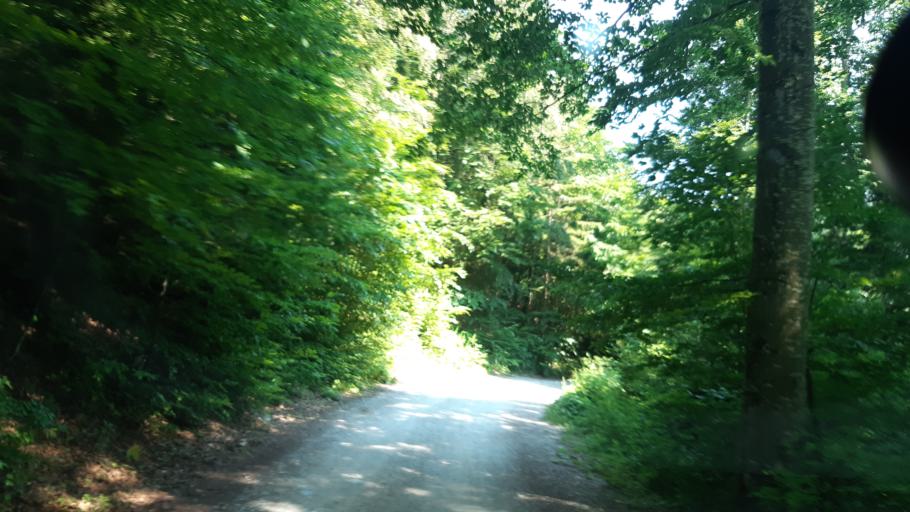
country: SI
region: Trzic
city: Bistrica pri Trzicu
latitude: 46.3767
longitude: 14.2759
